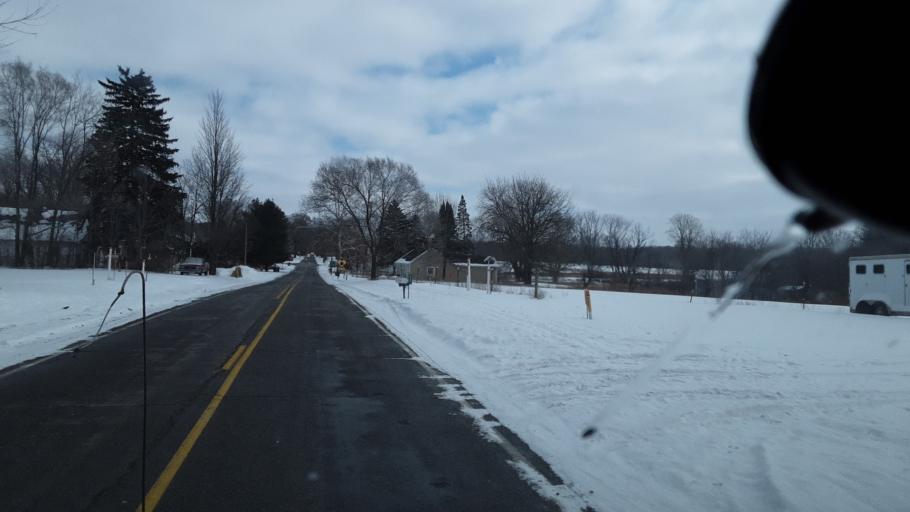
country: US
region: Michigan
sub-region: Ingham County
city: Leslie
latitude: 42.4753
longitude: -84.3202
